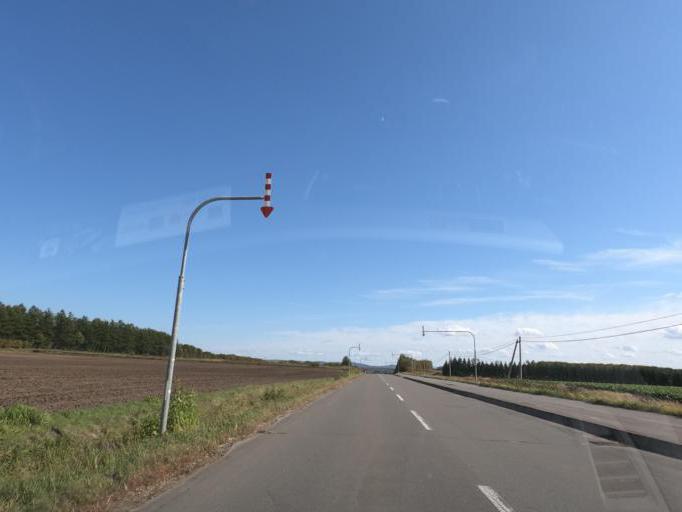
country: JP
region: Hokkaido
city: Otofuke
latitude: 43.2414
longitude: 143.2564
